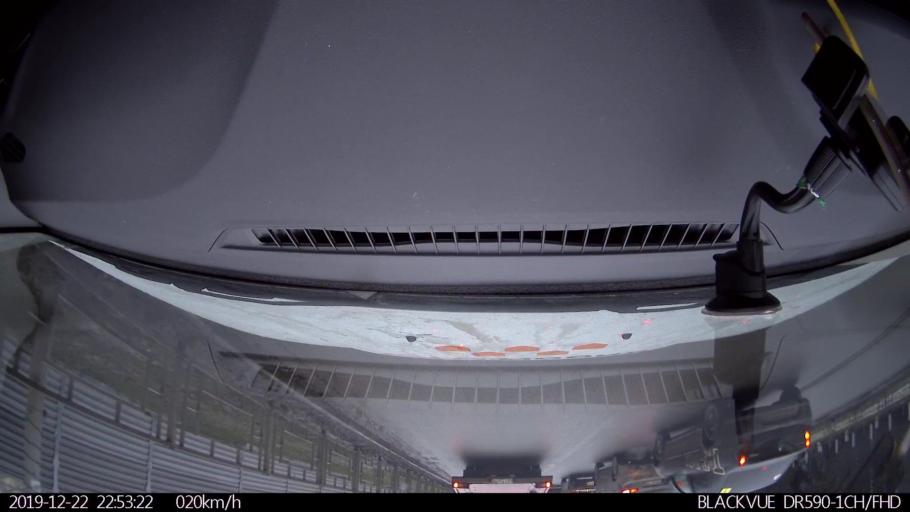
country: RU
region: Nizjnij Novgorod
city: Gorbatovka
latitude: 56.2428
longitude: 43.8514
